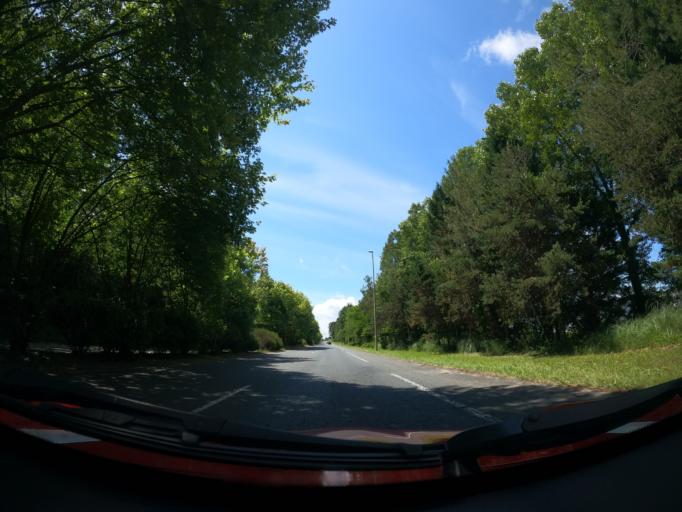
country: FR
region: Aquitaine
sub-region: Departement des Pyrenees-Atlantiques
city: Bayonne
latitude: 43.4697
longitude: -1.4930
